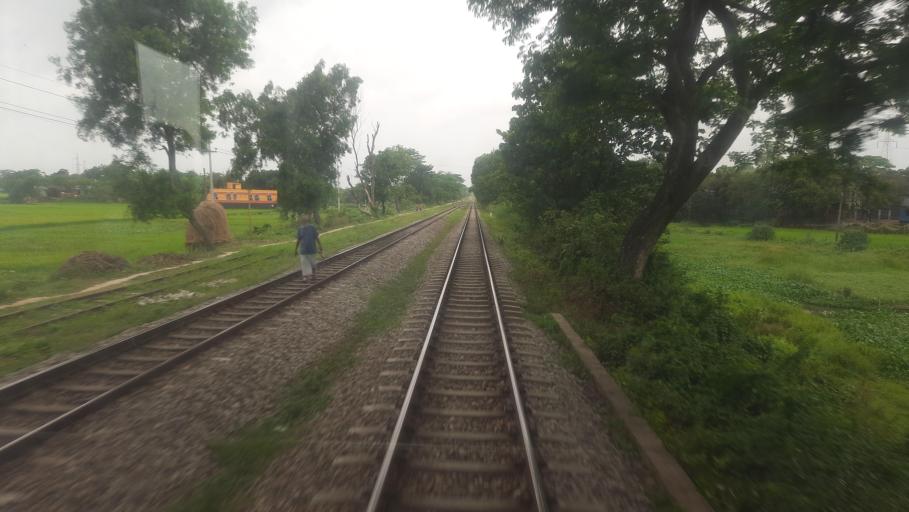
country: BD
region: Dhaka
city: Bhairab Bazar
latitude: 24.0262
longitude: 91.0175
